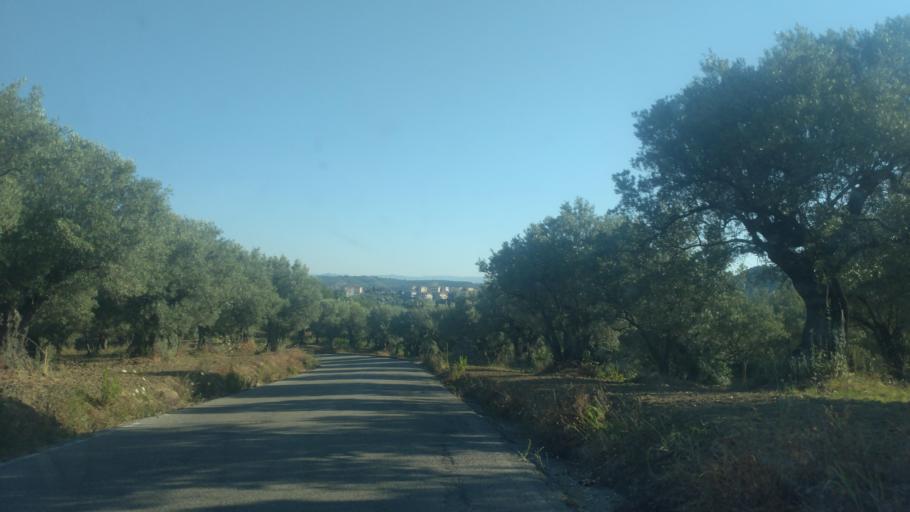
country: IT
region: Calabria
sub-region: Provincia di Catanzaro
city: Squillace
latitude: 38.7708
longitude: 16.5097
